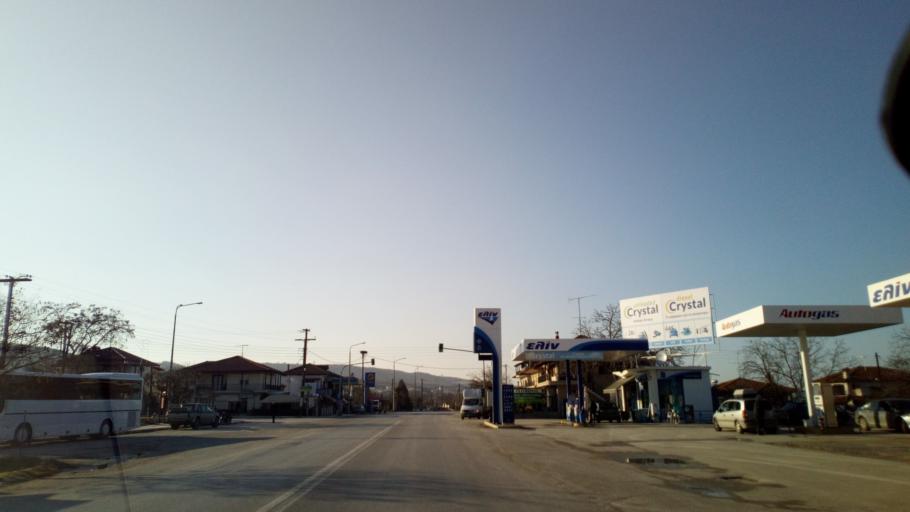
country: GR
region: Central Macedonia
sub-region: Nomos Thessalonikis
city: Gerakarou
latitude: 40.6356
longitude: 23.1927
